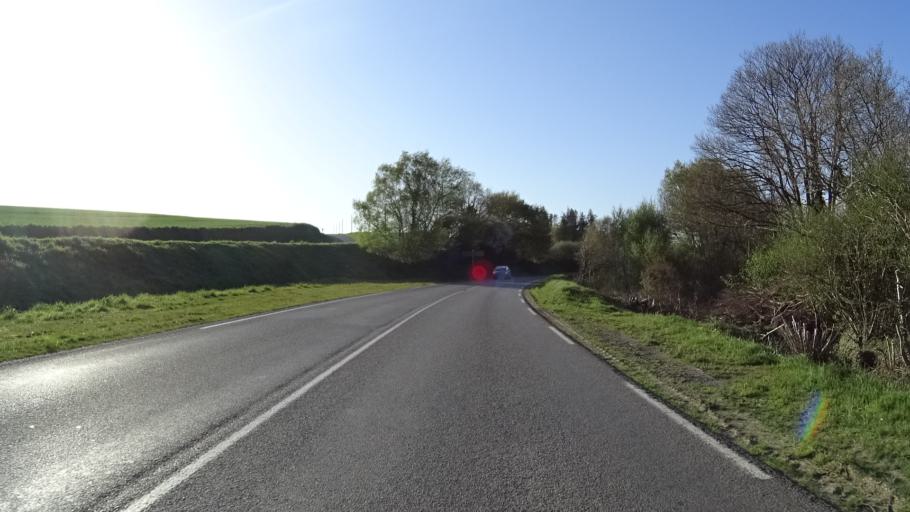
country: FR
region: Brittany
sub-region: Departement du Finistere
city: Sizun
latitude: 48.4156
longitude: -4.0991
